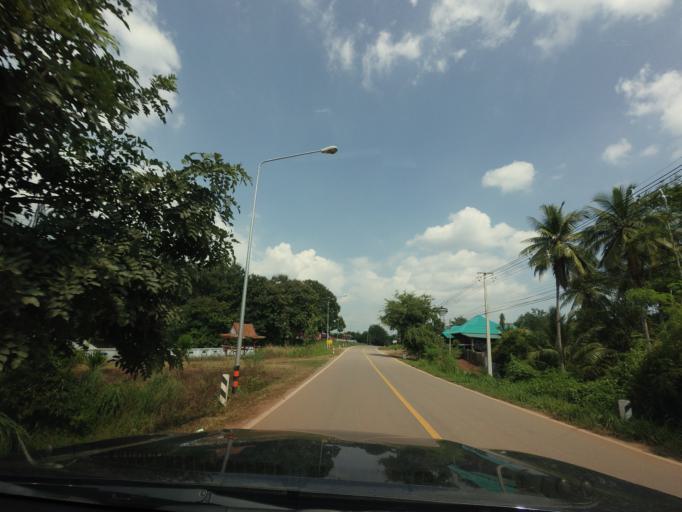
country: TH
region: Uttaradit
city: Ban Khok
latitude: 18.0213
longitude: 101.0569
